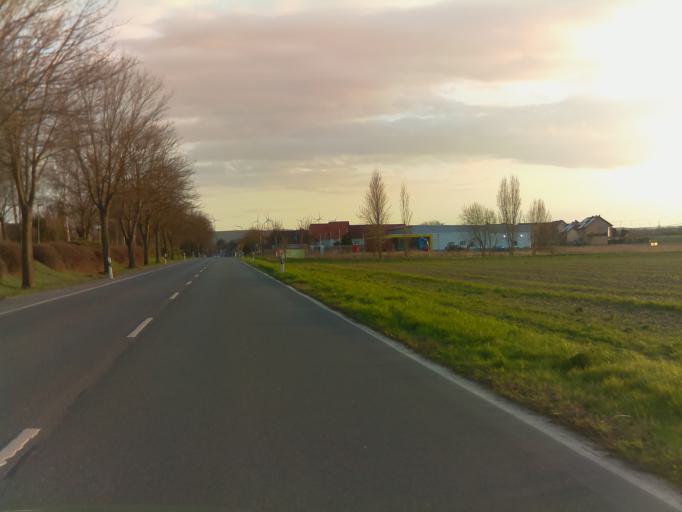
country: DE
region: Rheinland-Pfalz
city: Armsheim
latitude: 49.8165
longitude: 8.0600
